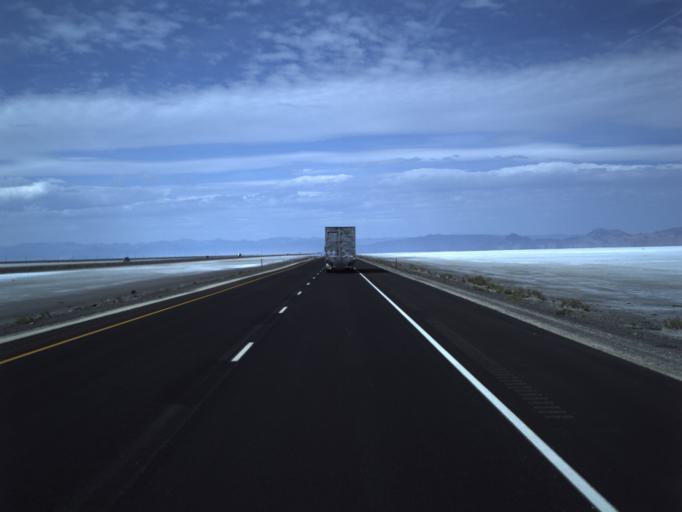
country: US
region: Utah
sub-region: Tooele County
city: Wendover
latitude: 40.7344
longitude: -113.6146
